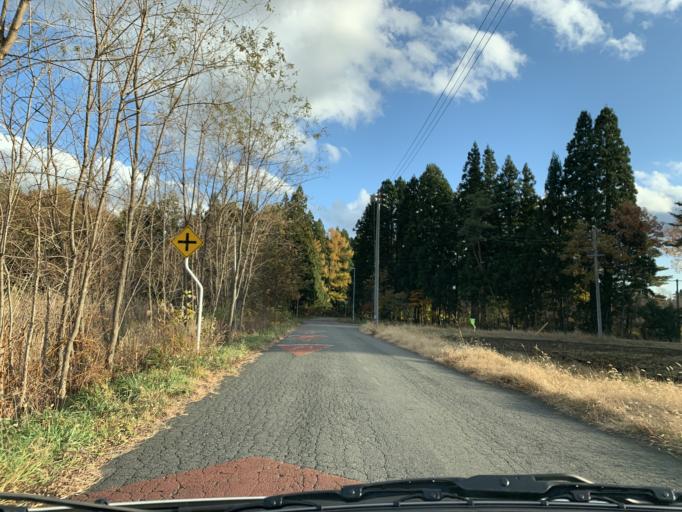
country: JP
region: Iwate
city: Mizusawa
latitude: 39.1168
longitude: 140.9991
